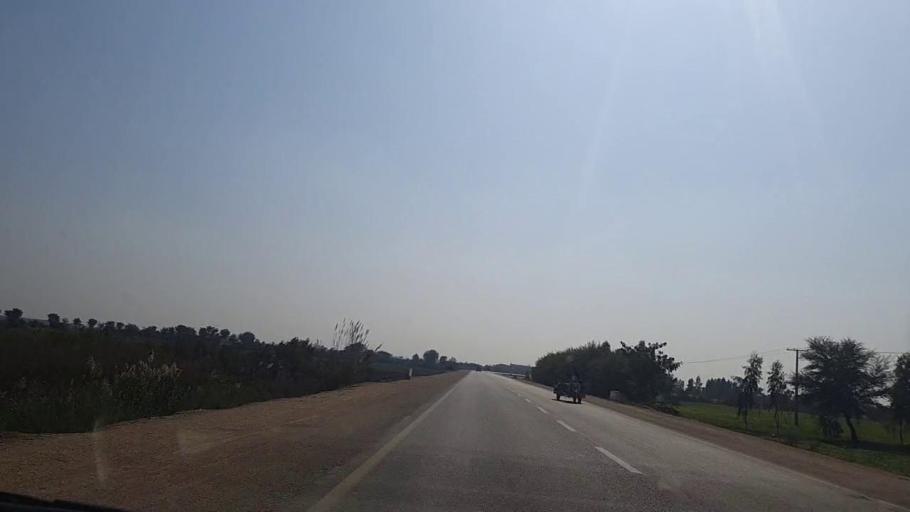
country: PK
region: Sindh
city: Sakrand
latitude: 26.0013
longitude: 68.3937
